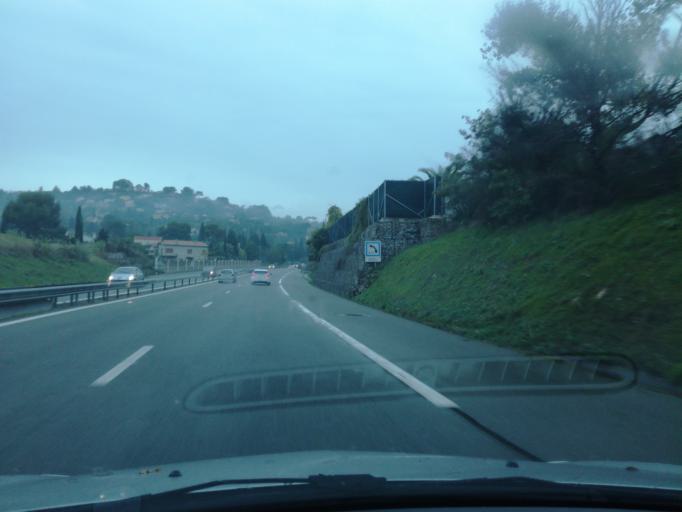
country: FR
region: Provence-Alpes-Cote d'Azur
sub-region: Departement des Alpes-Maritimes
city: Mougins
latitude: 43.5913
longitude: 7.0007
